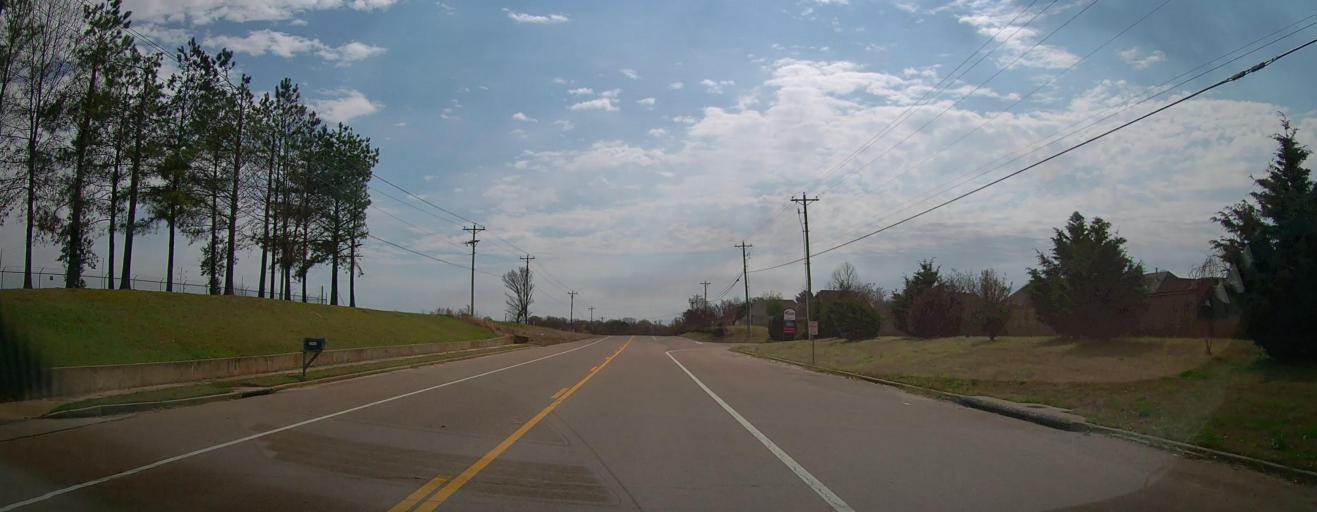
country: US
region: Mississippi
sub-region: De Soto County
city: Olive Branch
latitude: 34.9780
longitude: -89.8504
